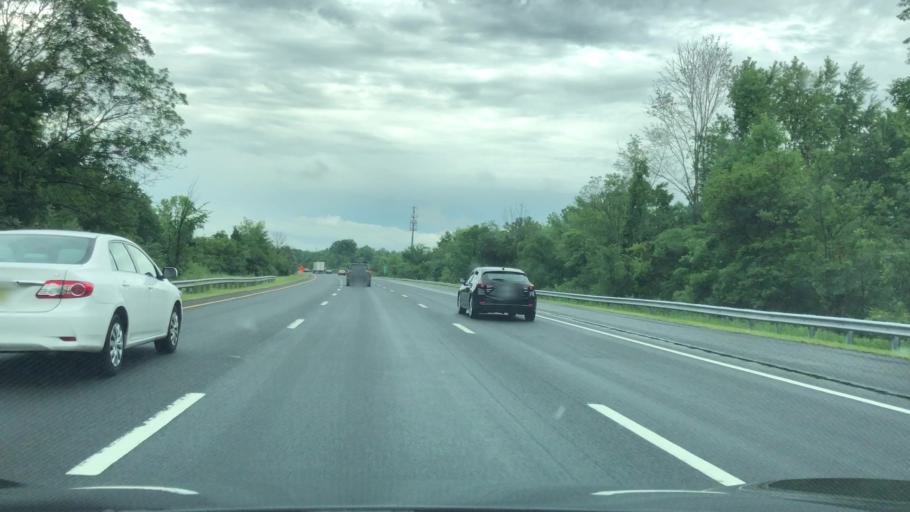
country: US
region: New Jersey
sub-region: Mercer County
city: Lawrenceville
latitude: 40.2901
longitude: -74.7670
